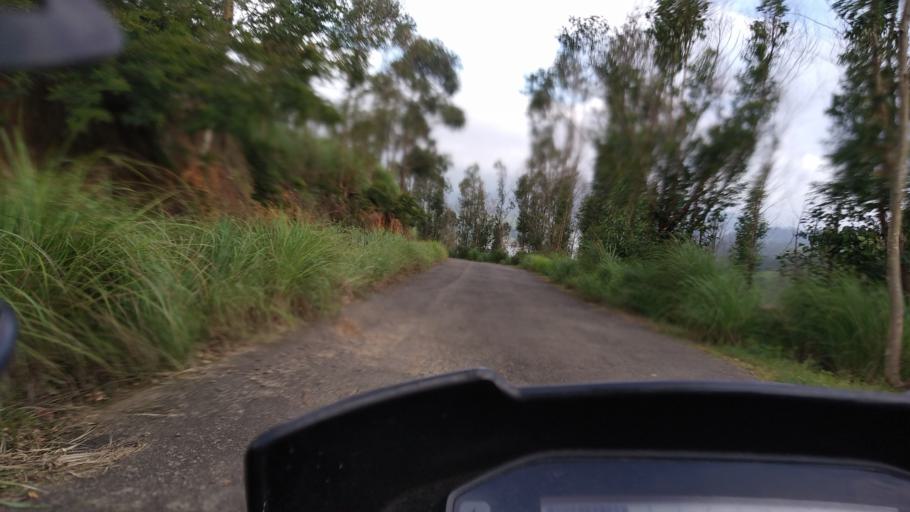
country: IN
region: Kerala
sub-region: Idukki
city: Munnar
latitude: 10.0366
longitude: 77.1851
